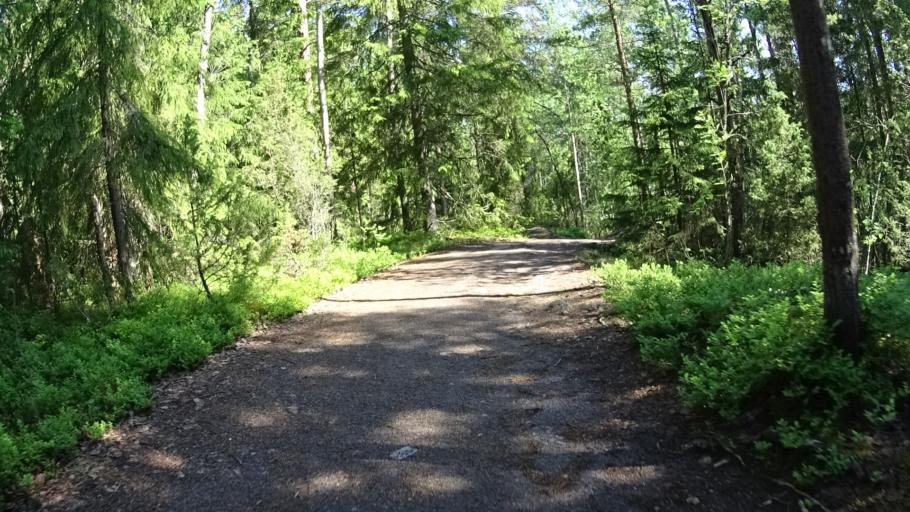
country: FI
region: Uusimaa
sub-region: Helsinki
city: Kauniainen
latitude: 60.3324
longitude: 24.6845
